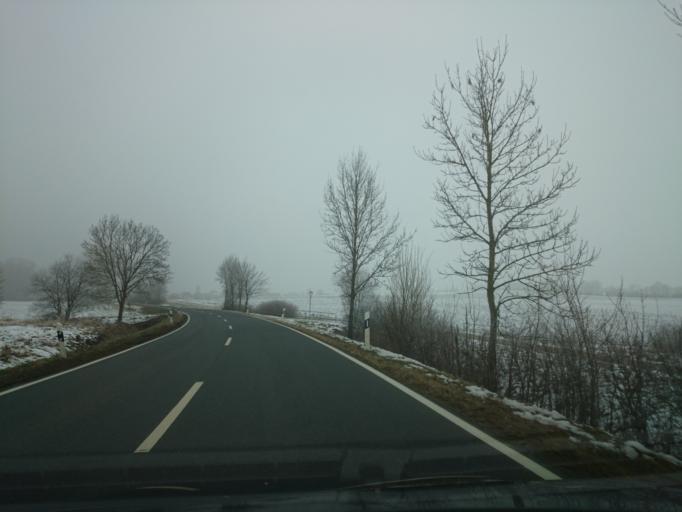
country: DE
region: Bavaria
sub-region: Regierungsbezirk Mittelfranken
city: Thalmassing
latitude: 49.1170
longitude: 11.2733
